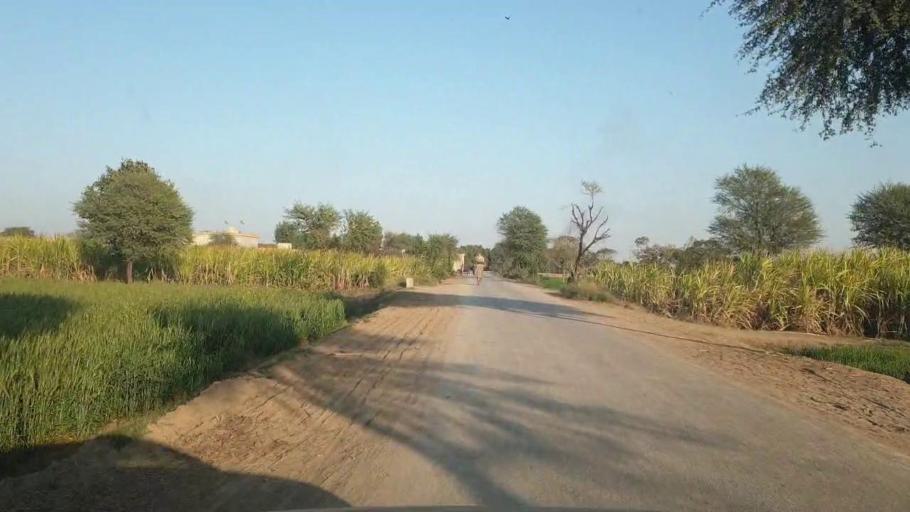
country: PK
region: Sindh
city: Tando Allahyar
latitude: 25.3539
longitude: 68.7074
